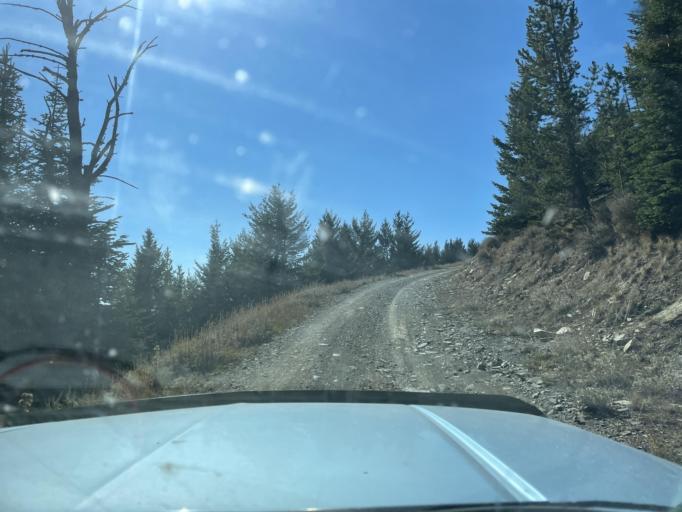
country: US
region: Montana
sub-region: Broadwater County
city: Townsend
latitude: 46.4984
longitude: -111.2606
